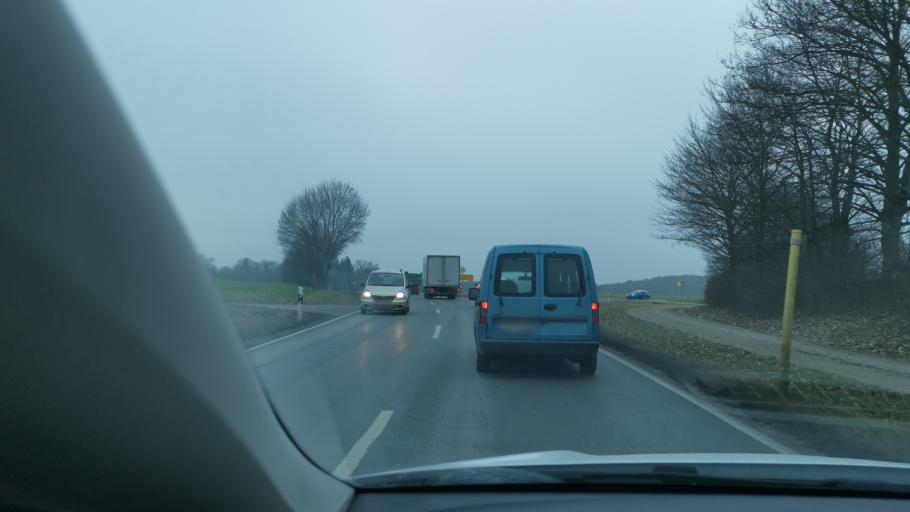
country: DE
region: Bavaria
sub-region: Swabia
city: Thierhaupten
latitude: 48.5754
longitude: 10.9075
